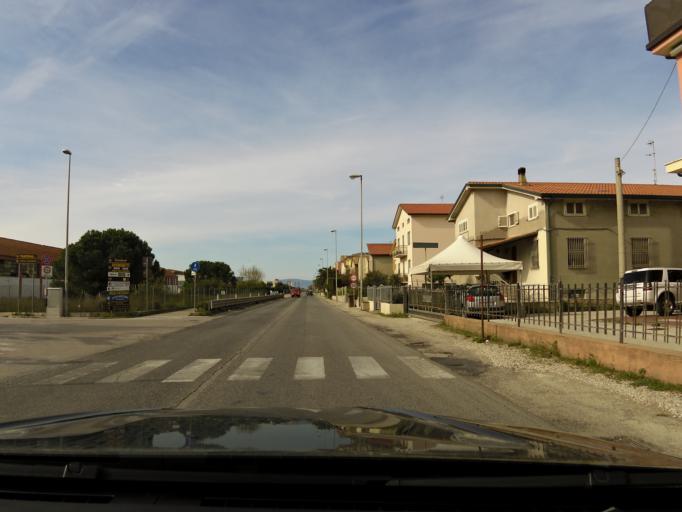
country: IT
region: The Marches
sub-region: Provincia di Macerata
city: Porto Potenza Picena
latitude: 43.3811
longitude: 13.6880
